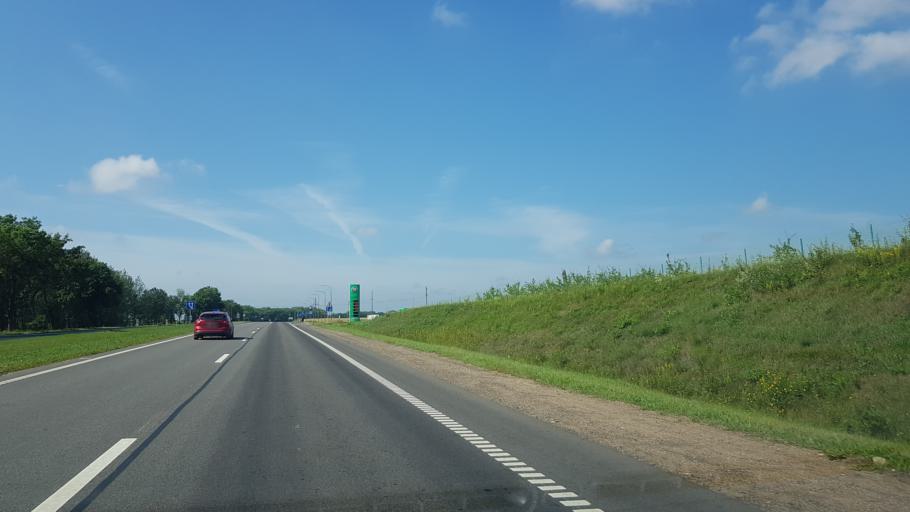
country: BY
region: Minsk
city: Dzyarzhynsk
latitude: 53.6961
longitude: 27.1780
